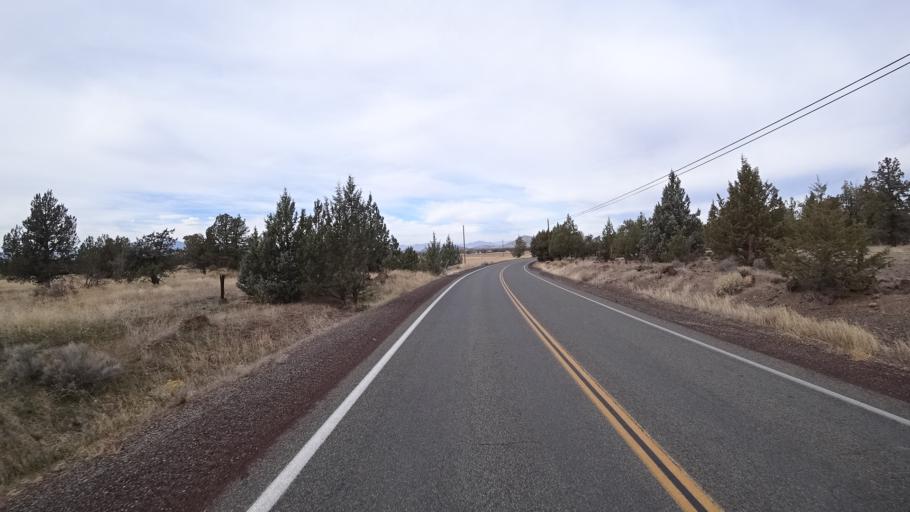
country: US
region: California
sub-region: Siskiyou County
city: Montague
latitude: 41.6170
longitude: -122.3724
